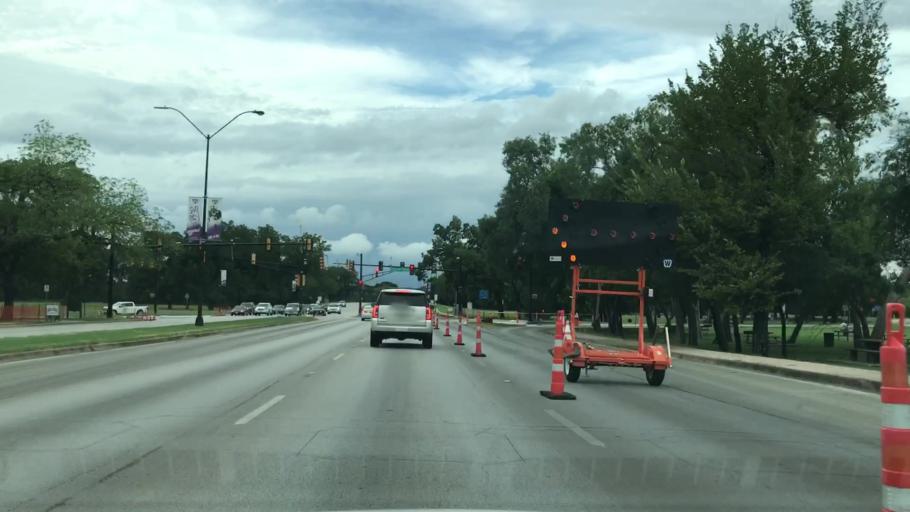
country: US
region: Texas
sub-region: Tarrant County
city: Fort Worth
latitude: 32.7211
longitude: -97.3612
